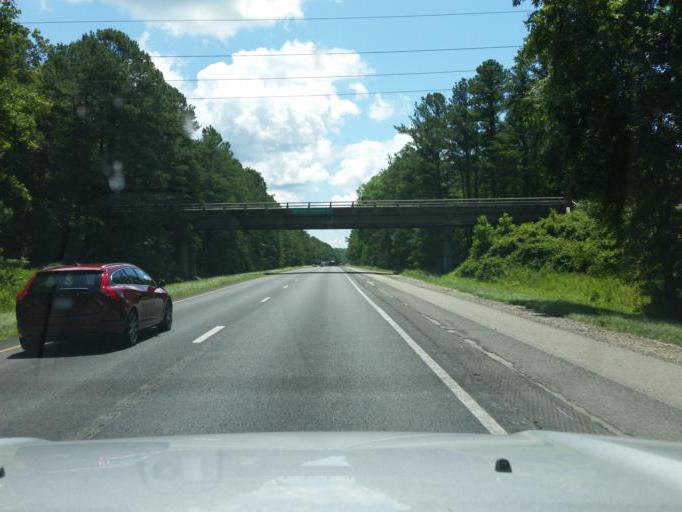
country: US
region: Virginia
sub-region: New Kent County
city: New Kent
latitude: 37.4603
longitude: -76.8836
